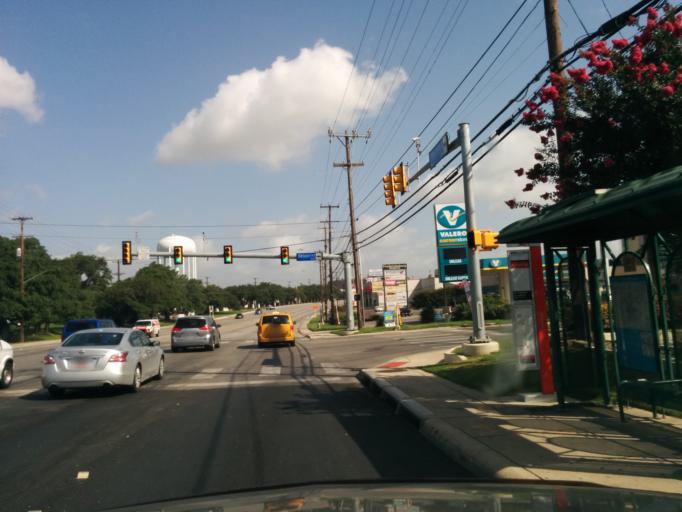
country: US
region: Texas
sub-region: Bexar County
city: Balcones Heights
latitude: 29.5140
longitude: -98.5701
